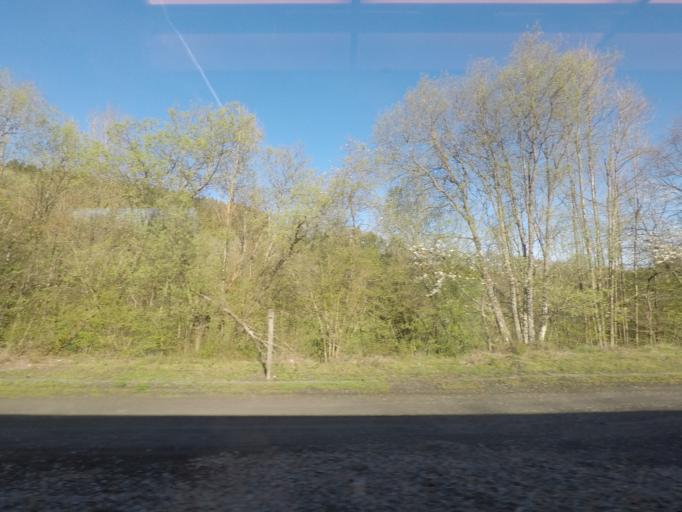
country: BE
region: Wallonia
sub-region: Province du Luxembourg
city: Tellin
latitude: 50.0887
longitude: 5.2786
